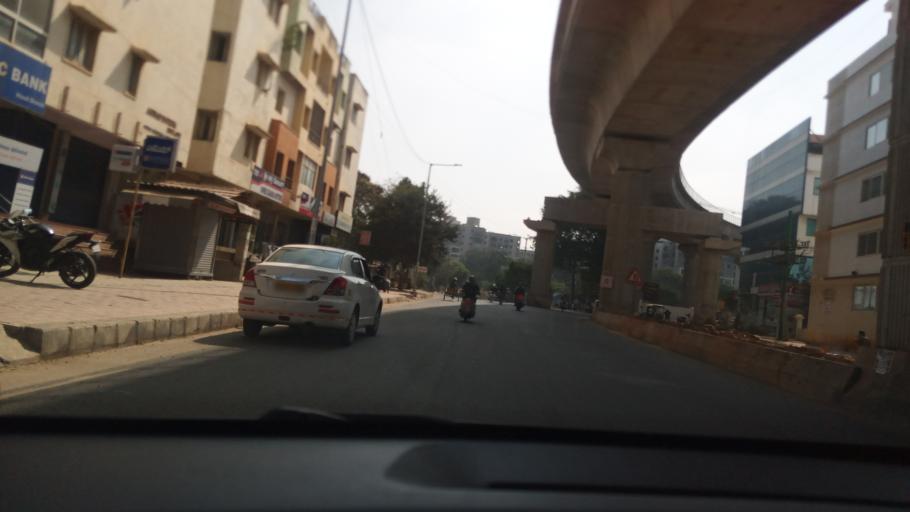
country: IN
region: Karnataka
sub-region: Bangalore Rural
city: Hoskote
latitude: 12.9923
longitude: 77.7130
